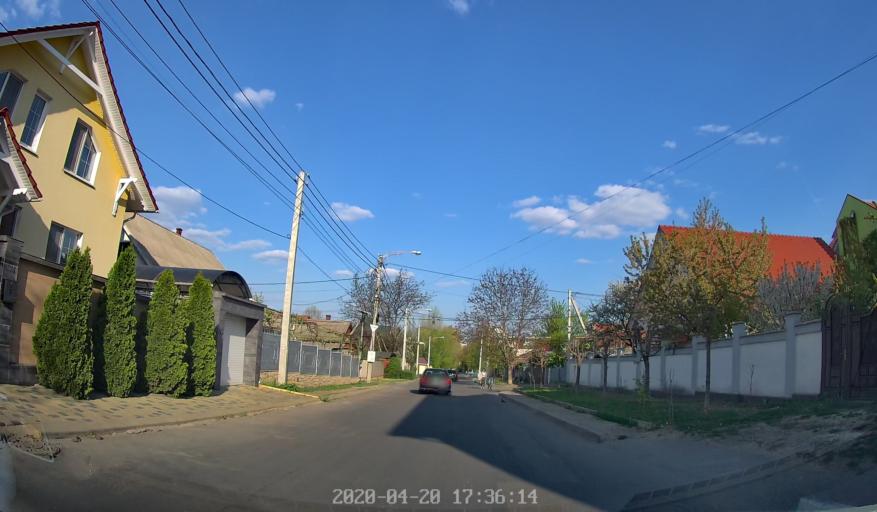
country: MD
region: Chisinau
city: Chisinau
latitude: 46.9890
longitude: 28.8619
